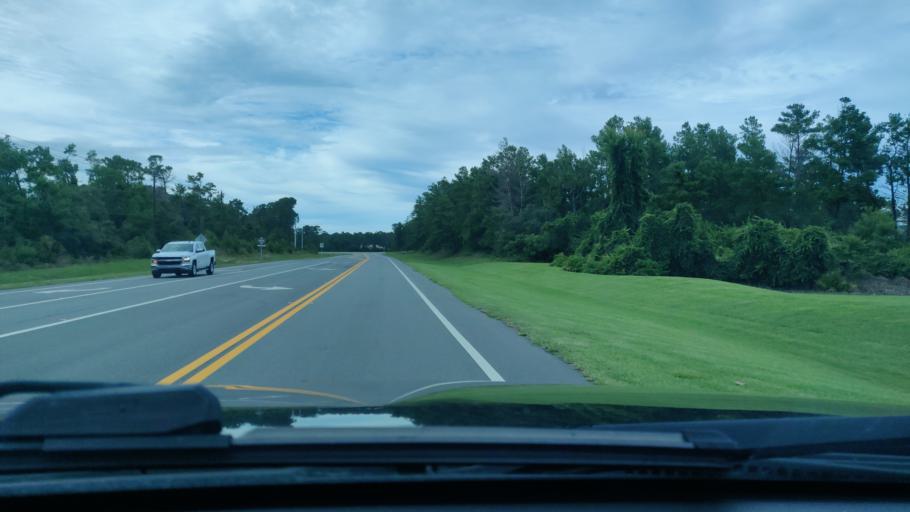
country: US
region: Florida
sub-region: Flagler County
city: Flagler Beach
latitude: 29.5275
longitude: -81.1702
